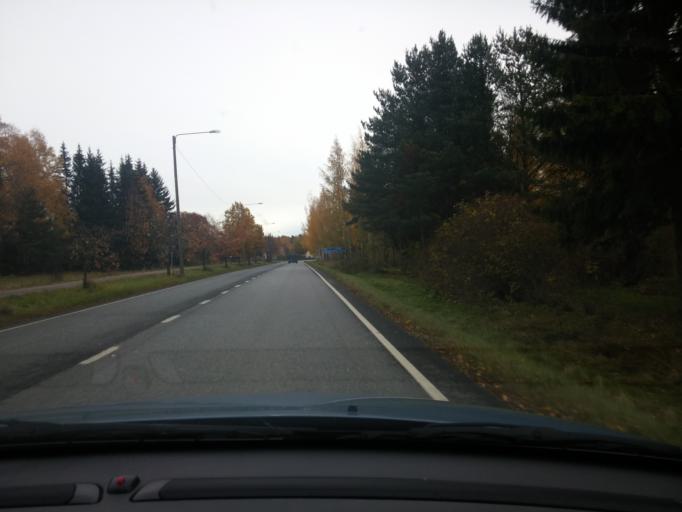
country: FI
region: Haeme
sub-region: Forssa
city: Tammela
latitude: 60.8066
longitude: 23.7902
